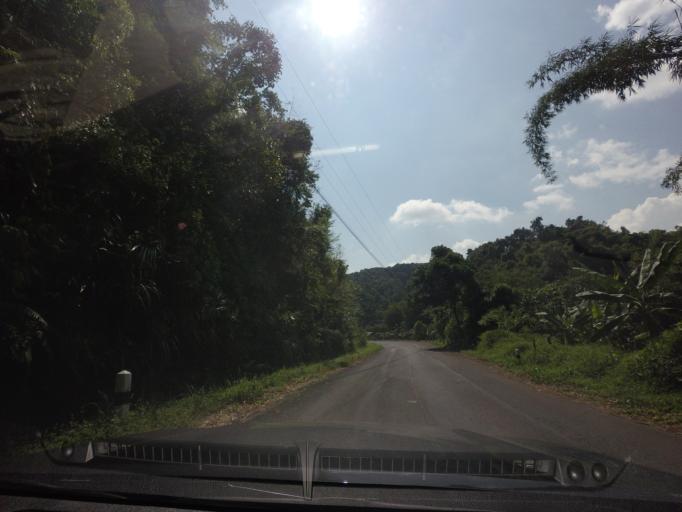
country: TH
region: Nan
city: Bo Kluea
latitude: 19.0620
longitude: 101.0989
